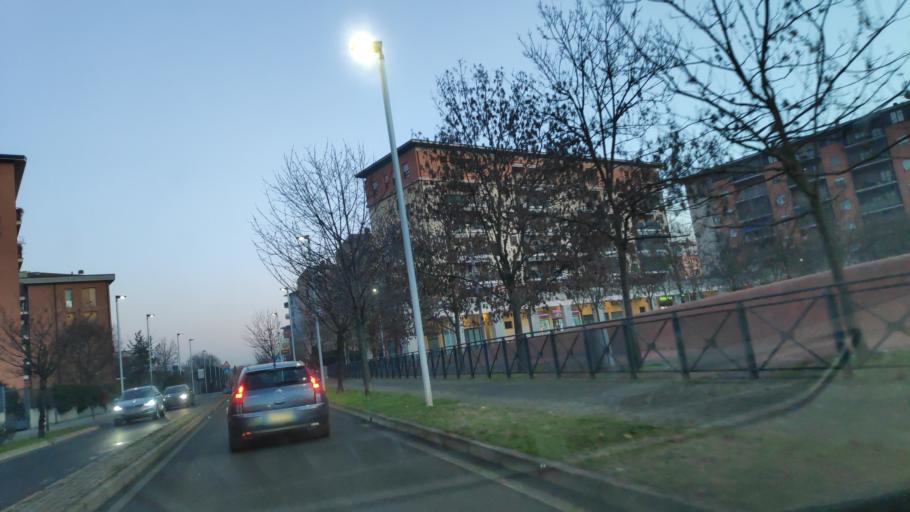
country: IT
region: Lombardy
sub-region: Citta metropolitana di Milano
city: Rozzano
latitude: 45.3818
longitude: 9.1616
